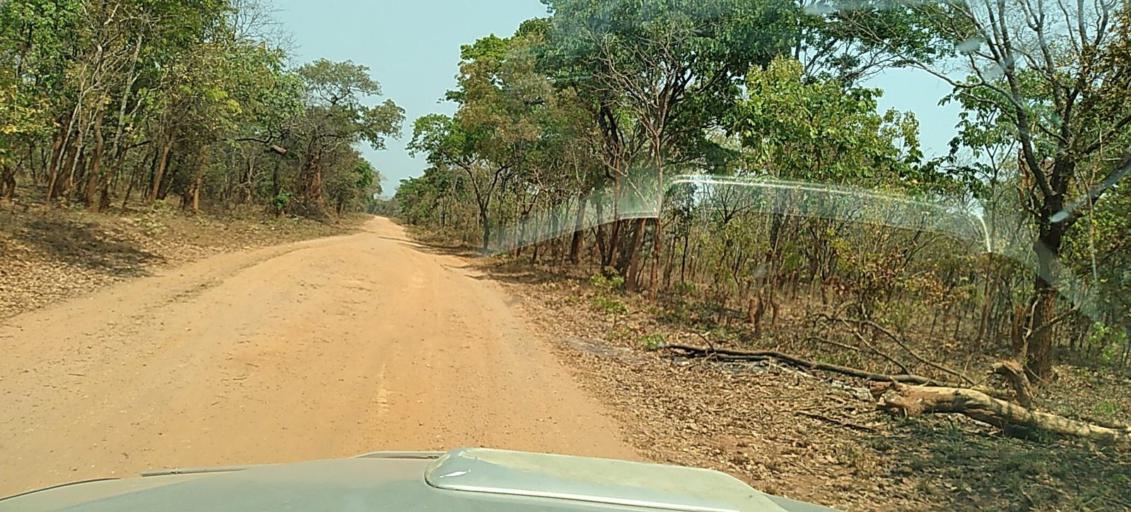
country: ZM
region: North-Western
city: Kasempa
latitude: -13.6875
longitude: 26.3209
